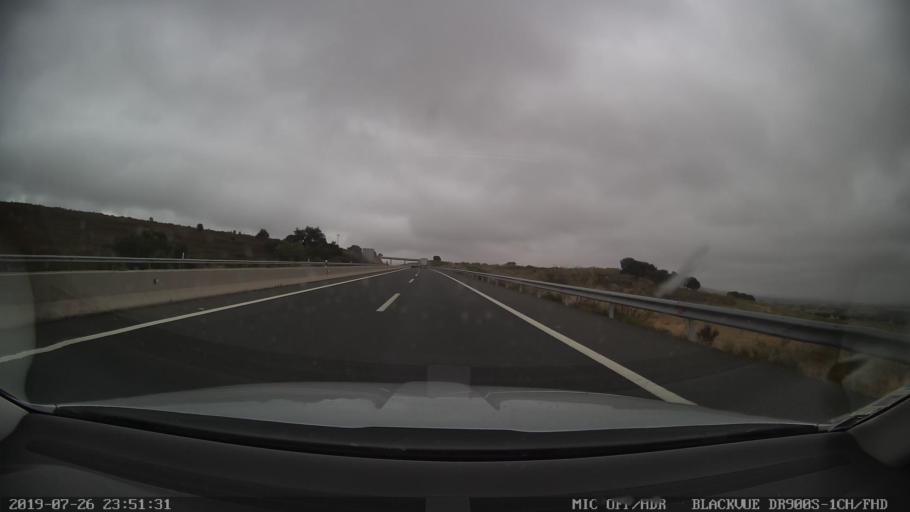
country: ES
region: Extremadura
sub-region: Provincia de Caceres
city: Jaraicejo
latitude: 39.6630
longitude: -5.7689
